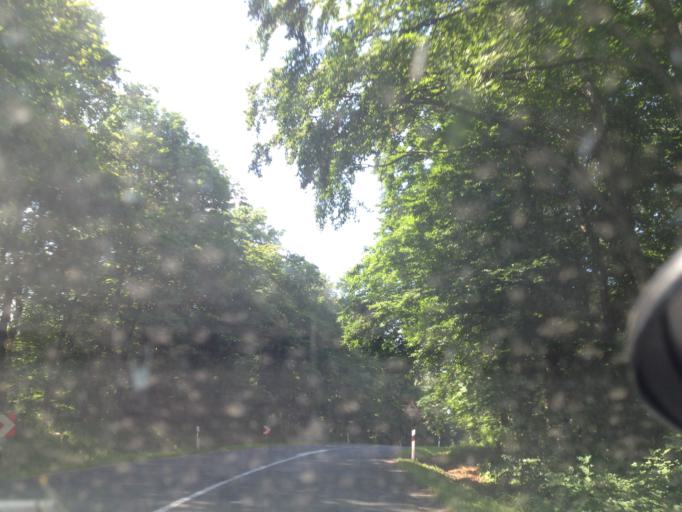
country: HU
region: Veszprem
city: Urkut
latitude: 47.1911
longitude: 17.6432
